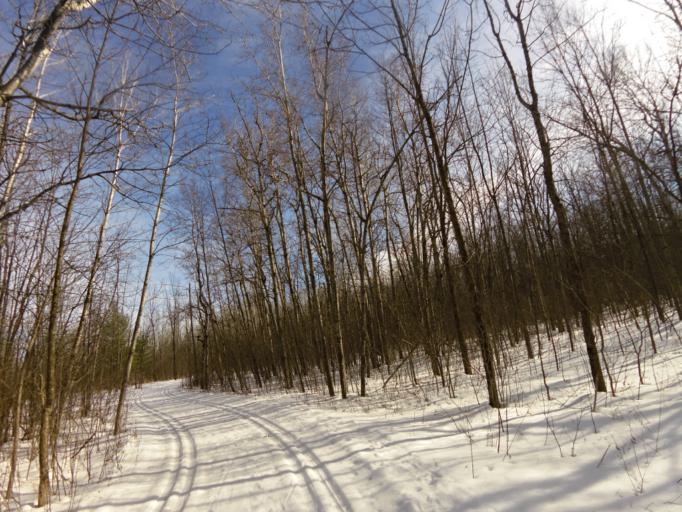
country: CA
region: Quebec
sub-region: Outaouais
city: Gatineau
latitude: 45.4562
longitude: -75.7726
